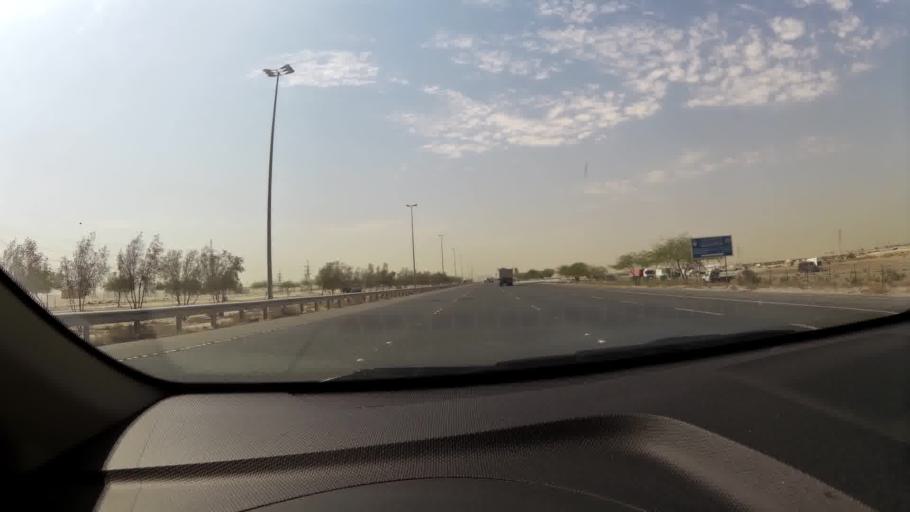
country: KW
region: Al Ahmadi
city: Al Fahahil
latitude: 28.7498
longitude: 48.2820
